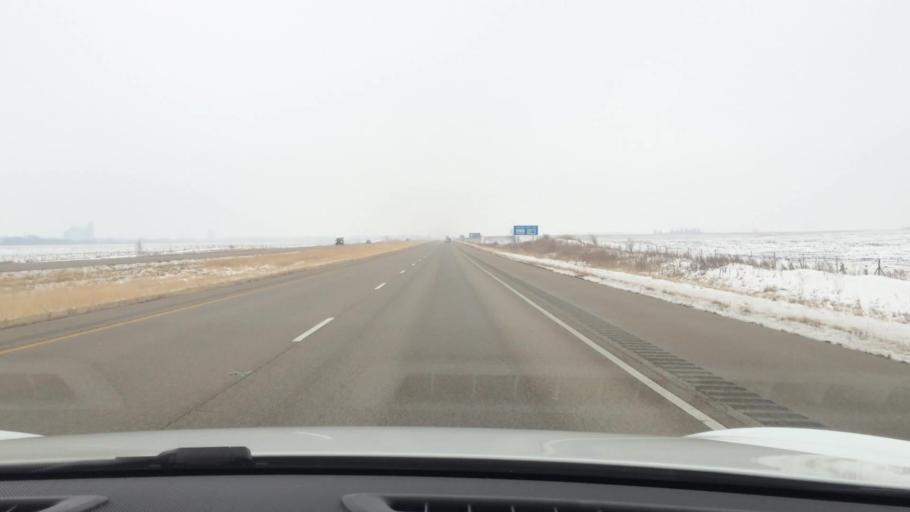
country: US
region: Illinois
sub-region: McLean County
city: Le Roy
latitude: 40.3542
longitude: -88.7986
